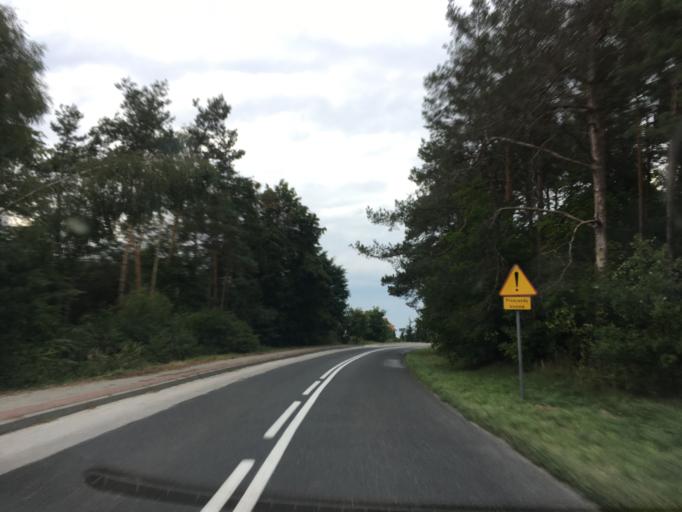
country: PL
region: Lodz Voivodeship
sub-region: Powiat radomszczanski
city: Przedborz
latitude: 51.0106
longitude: 19.8935
